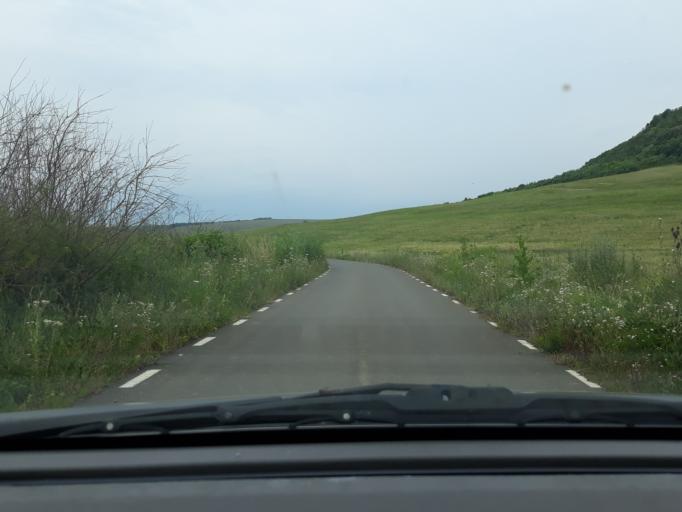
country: RO
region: Salaj
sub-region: Comuna Dobrin
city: Dobrin
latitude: 47.2780
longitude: 23.0823
